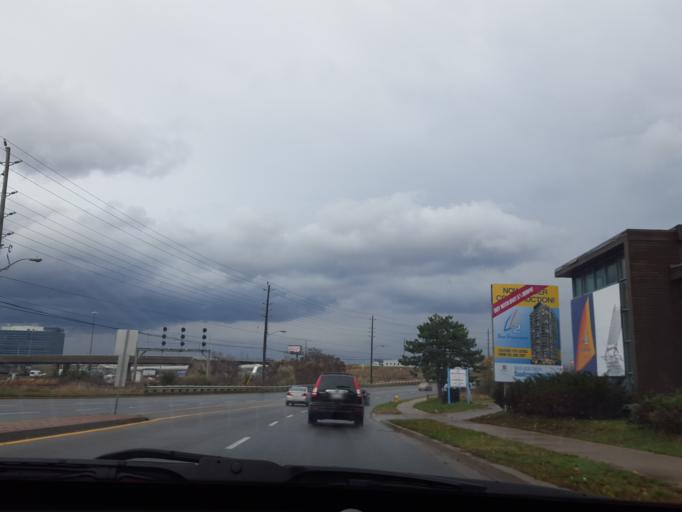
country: CA
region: Ontario
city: Ajax
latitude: 43.8280
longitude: -79.0908
